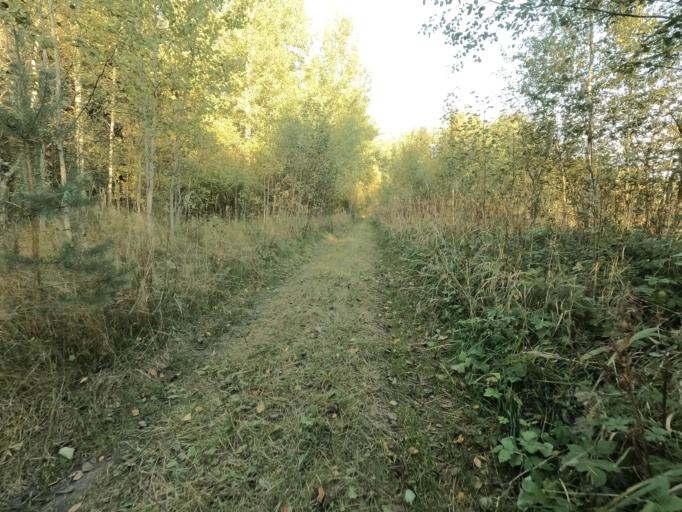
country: RU
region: Leningrad
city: Nikol'skoye
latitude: 59.7021
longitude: 30.7376
